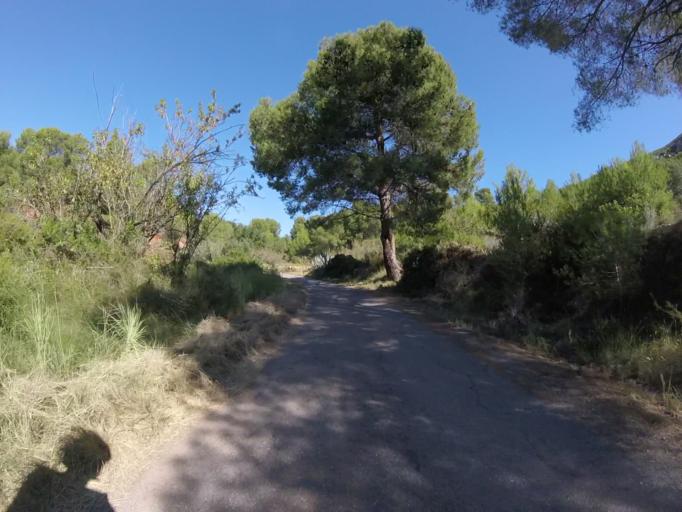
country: ES
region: Valencia
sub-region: Provincia de Castello
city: Cabanes
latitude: 40.1408
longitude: 0.1023
